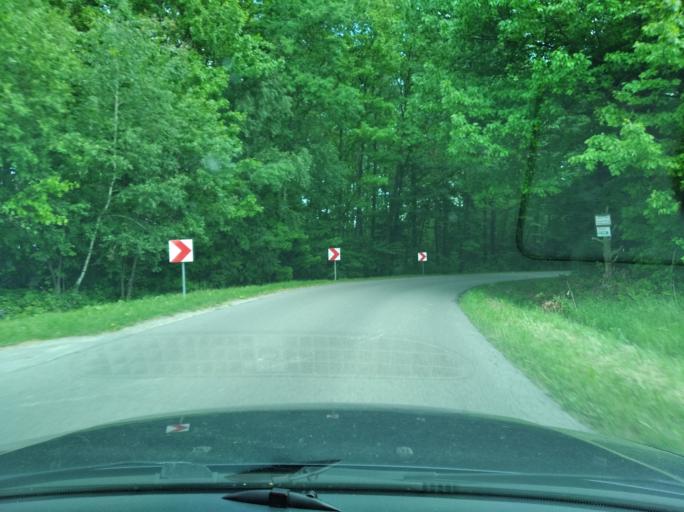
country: PL
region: Subcarpathian Voivodeship
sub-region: Powiat ropczycko-sedziszowski
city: Ropczyce
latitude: 50.0208
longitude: 21.6073
